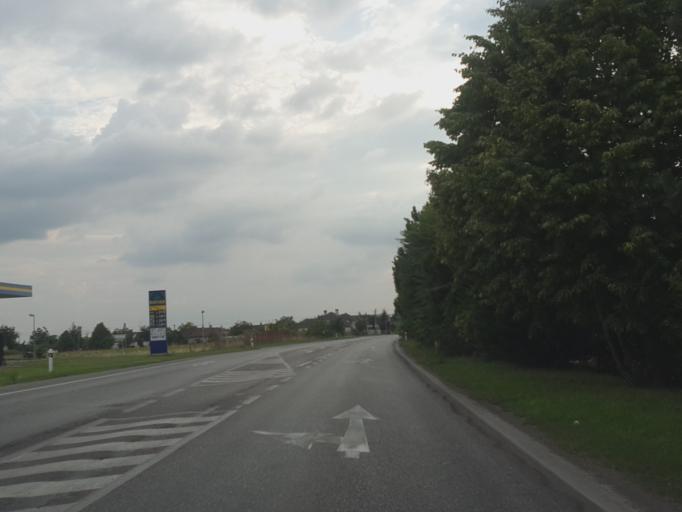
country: SK
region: Bratislavsky
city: Senec
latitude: 48.2085
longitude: 17.3646
